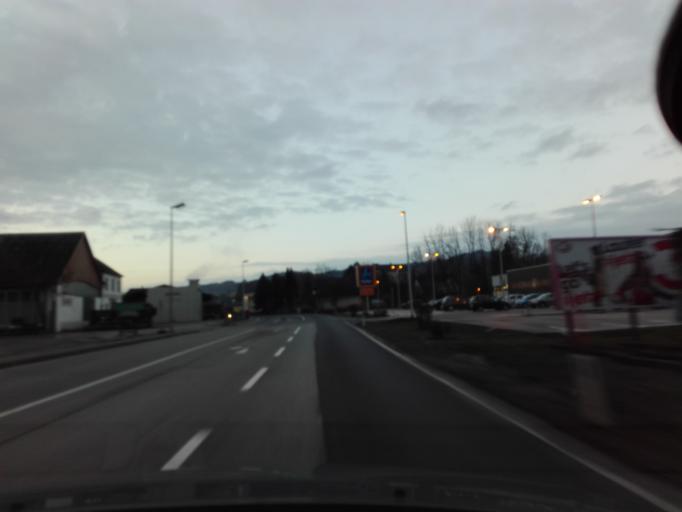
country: AT
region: Upper Austria
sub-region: Politischer Bezirk Perg
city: Bad Kreuzen
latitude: 48.2186
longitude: 14.8540
